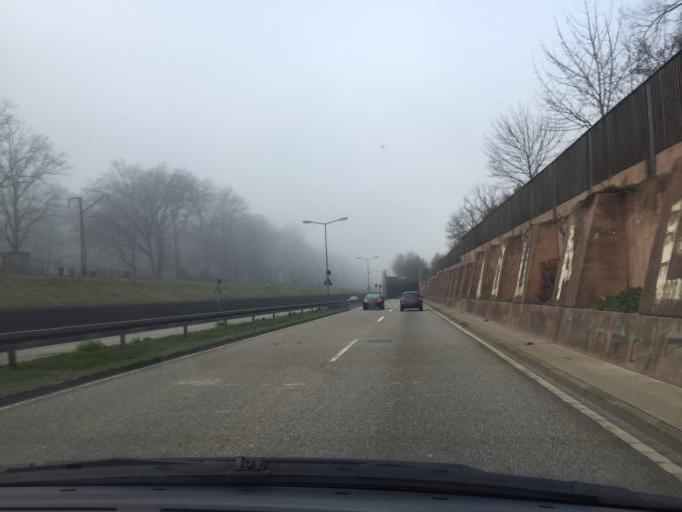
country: DE
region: Baden-Wuerttemberg
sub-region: Freiburg Region
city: Freiburg
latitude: 47.9848
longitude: 7.8808
